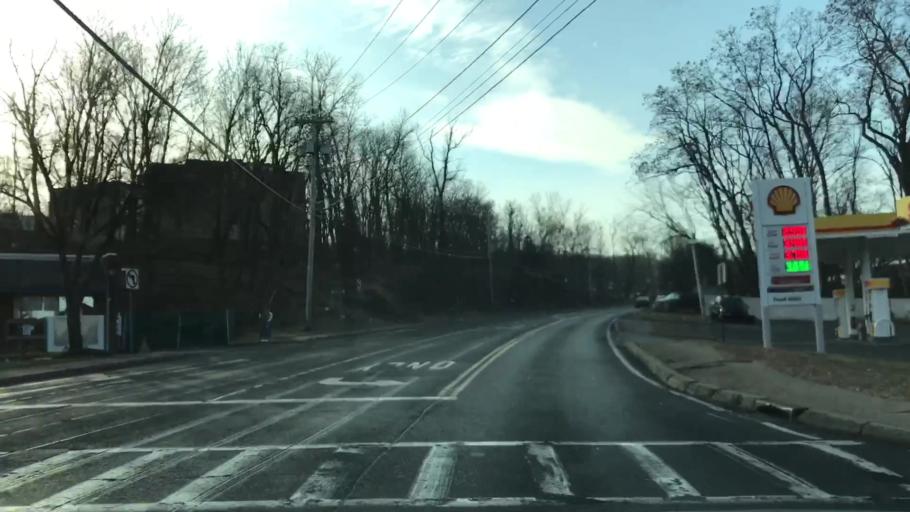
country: US
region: New York
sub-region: Rockland County
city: Valley Cottage
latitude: 41.1183
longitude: -73.9417
